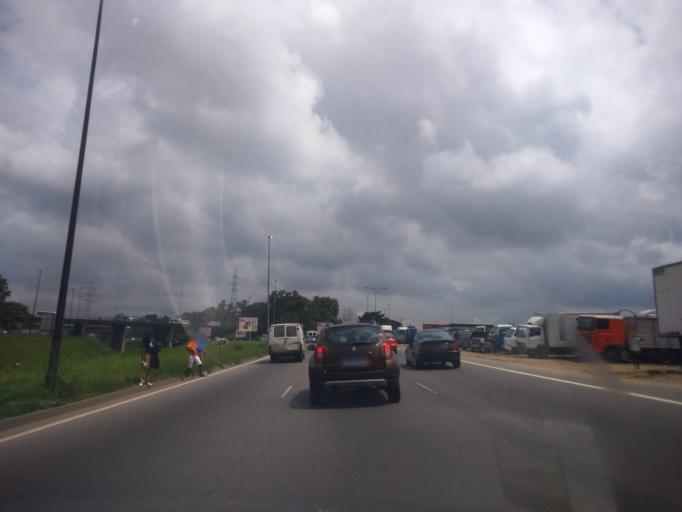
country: CI
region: Lagunes
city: Abobo
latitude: 5.3648
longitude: -4.0273
